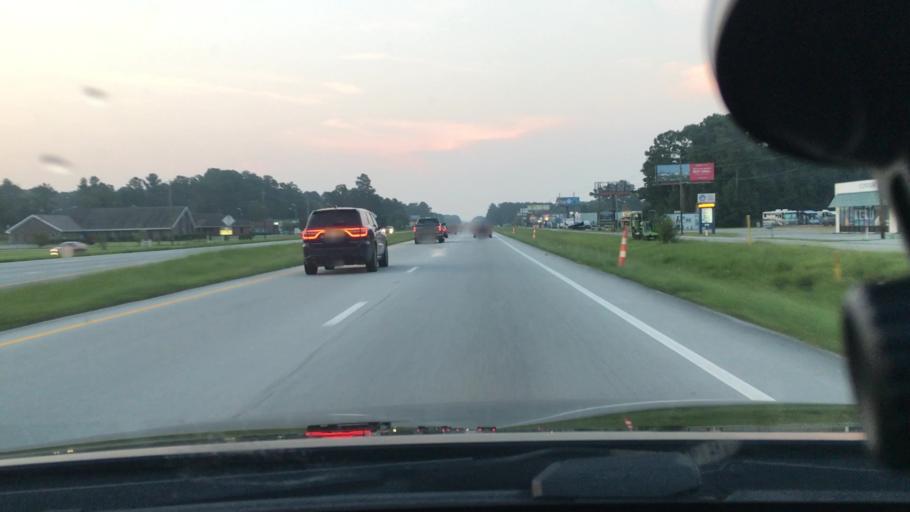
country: US
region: North Carolina
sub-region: Craven County
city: James City
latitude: 35.0640
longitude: -77.0221
